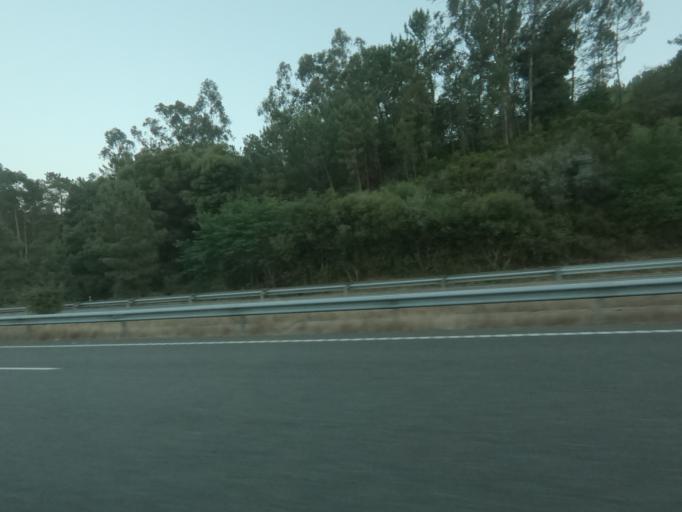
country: ES
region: Galicia
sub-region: Provincia de Pontevedra
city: Porrino
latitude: 42.1777
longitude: -8.5657
